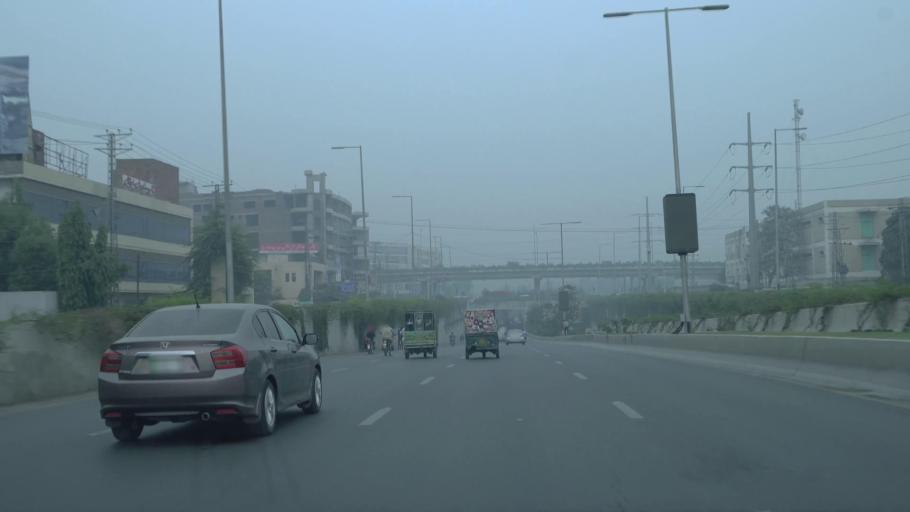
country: PK
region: Punjab
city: Lahore
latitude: 31.5036
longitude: 74.3289
